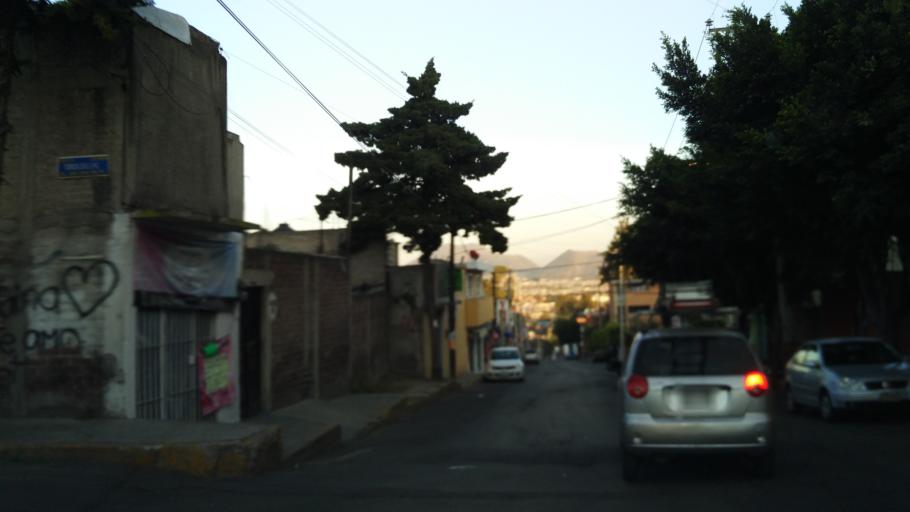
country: MX
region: Mexico City
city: Iztapalapa
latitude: 19.3303
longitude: -99.0879
